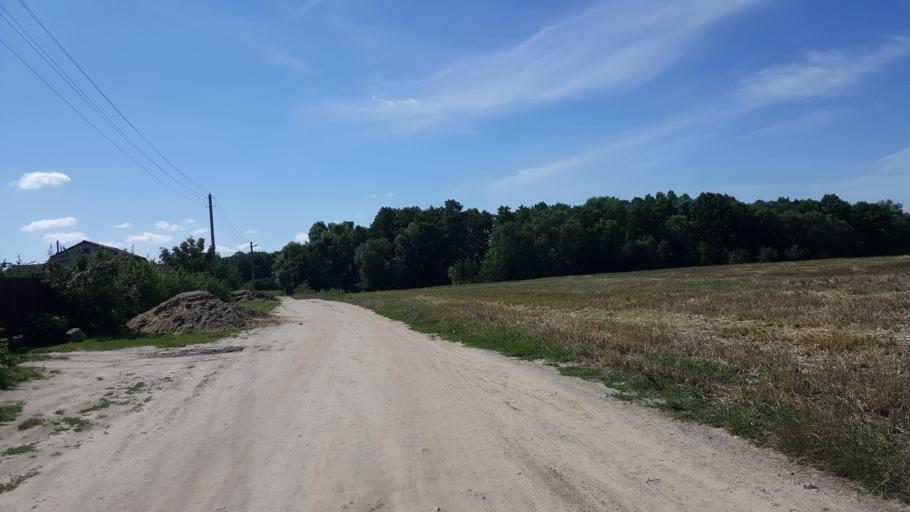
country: BY
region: Brest
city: Charnawchytsy
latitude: 52.2728
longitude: 23.7585
